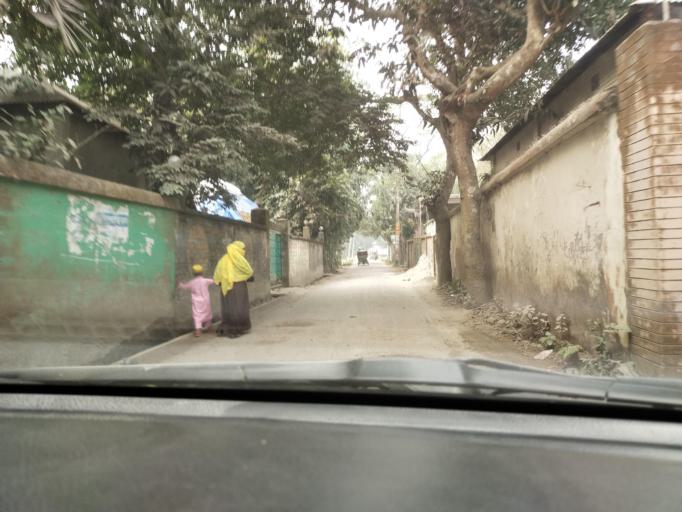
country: BD
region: Dhaka
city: Narsingdi
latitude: 24.0367
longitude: 90.7299
